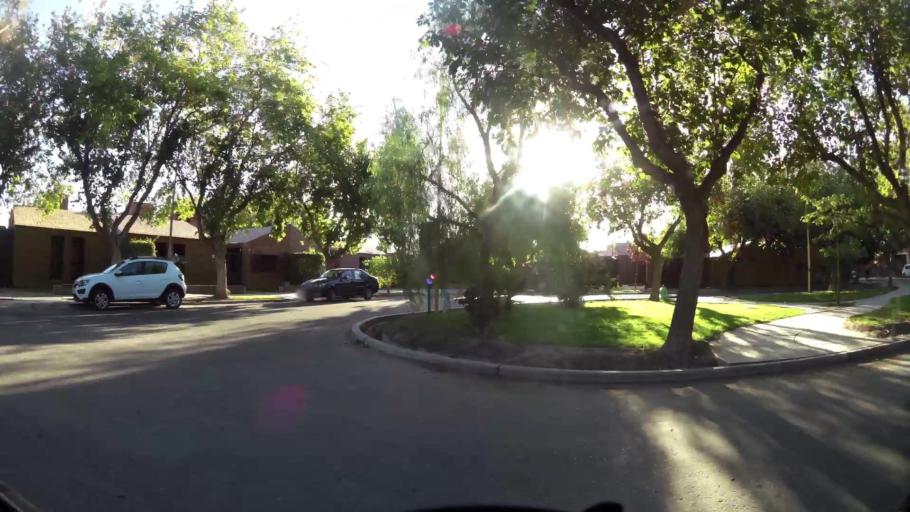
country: AR
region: San Juan
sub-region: Departamento de Santa Lucia
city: Santa Lucia
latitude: -31.5489
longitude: -68.5119
